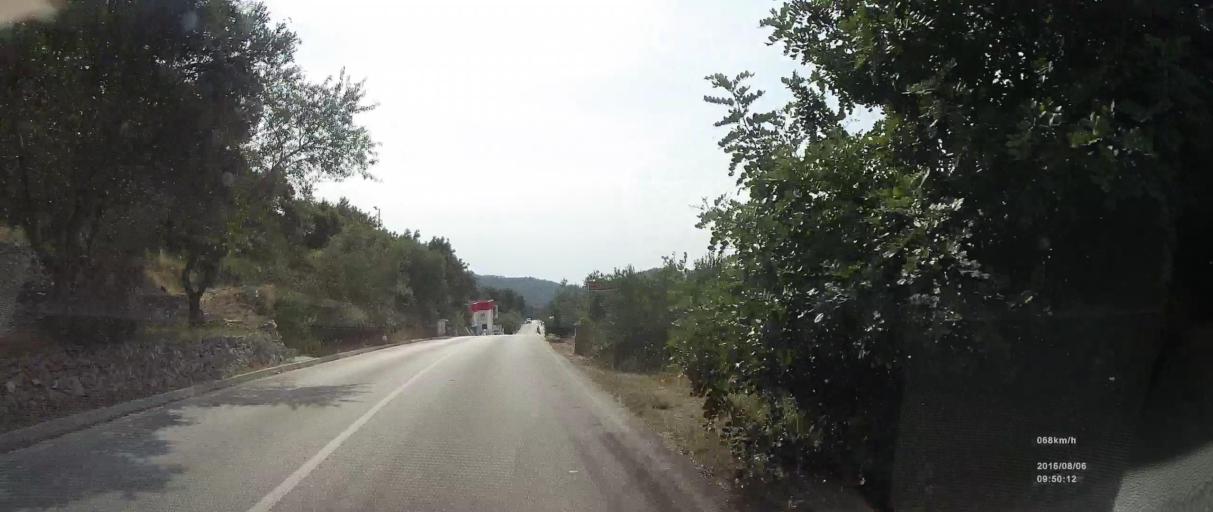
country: HR
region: Dubrovacko-Neretvanska
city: Blato
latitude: 42.7348
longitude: 17.5504
